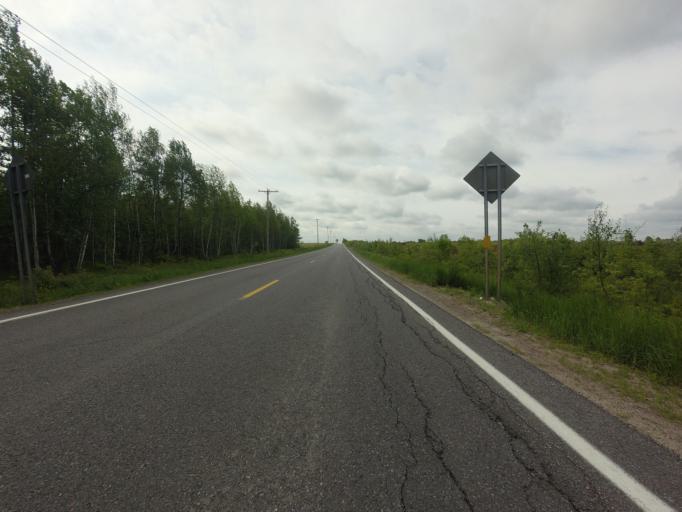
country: CA
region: Ontario
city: Cornwall
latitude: 44.7738
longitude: -74.6725
